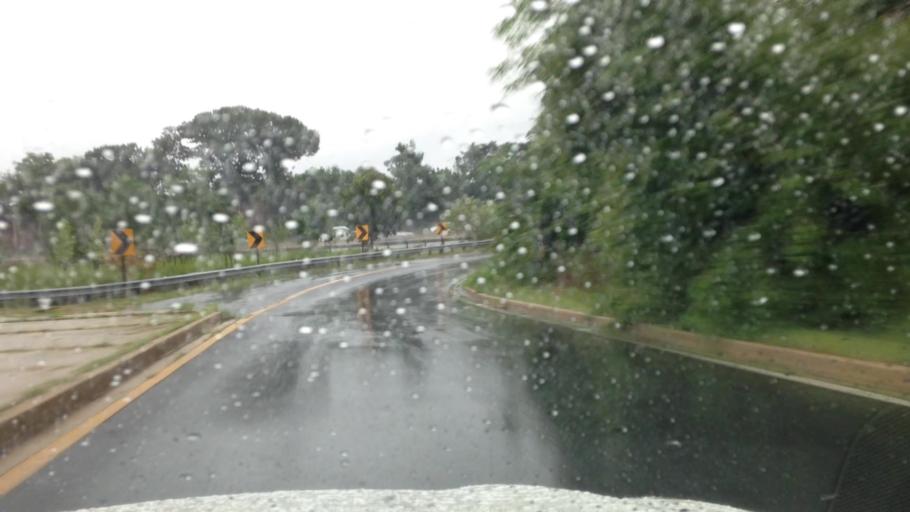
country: US
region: Maryland
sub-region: Anne Arundel County
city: South Gate
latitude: 39.1428
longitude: -76.6458
